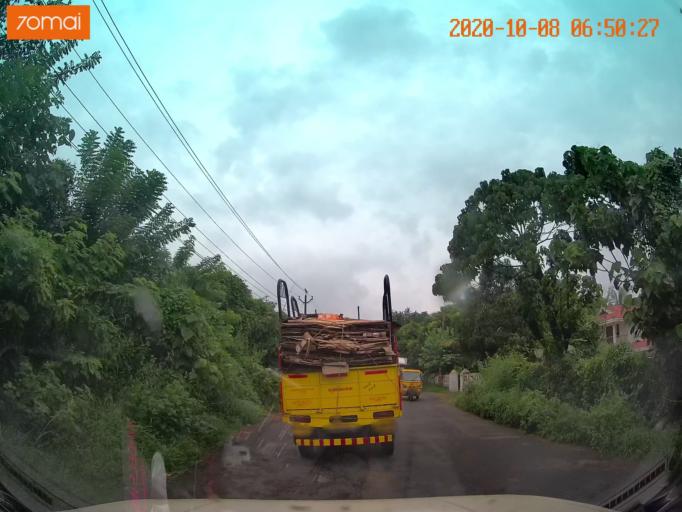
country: IN
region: Kerala
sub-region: Thrissur District
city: Kunnamkulam
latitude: 10.6879
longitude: 76.0994
